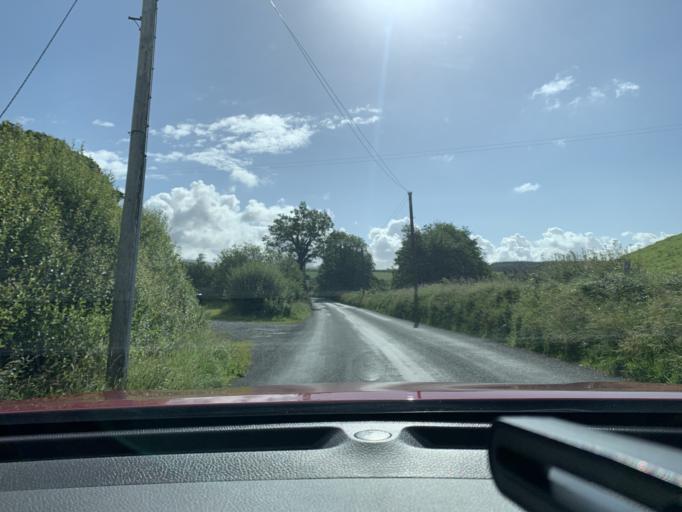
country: IE
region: Connaught
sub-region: Sligo
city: Strandhill
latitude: 54.3536
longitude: -8.6027
